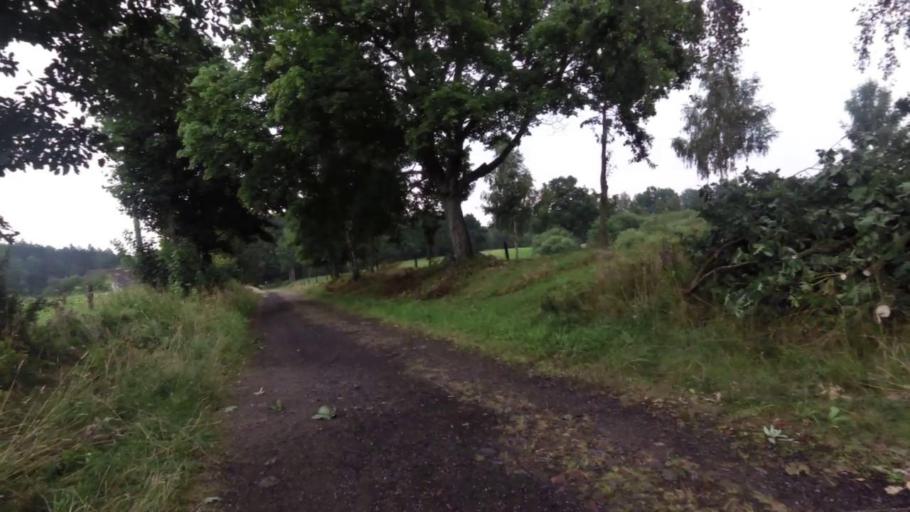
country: PL
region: West Pomeranian Voivodeship
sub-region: Powiat drawski
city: Czaplinek
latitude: 53.6054
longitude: 16.2712
